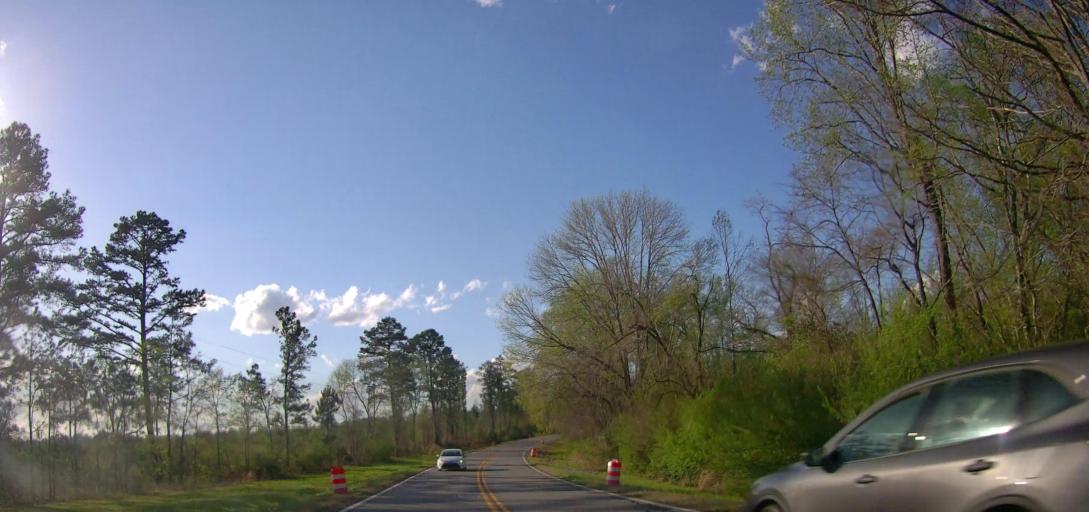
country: US
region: Georgia
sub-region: Baldwin County
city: Milledgeville
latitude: 33.1092
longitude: -83.2832
